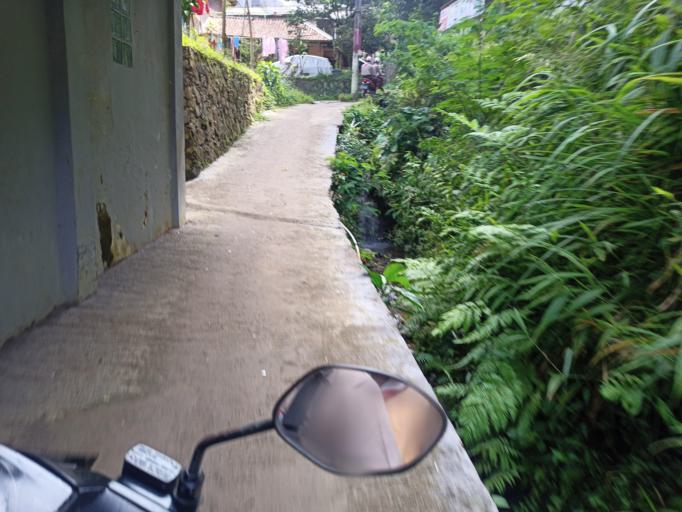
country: ID
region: West Java
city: Caringin
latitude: -6.6435
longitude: 106.9132
